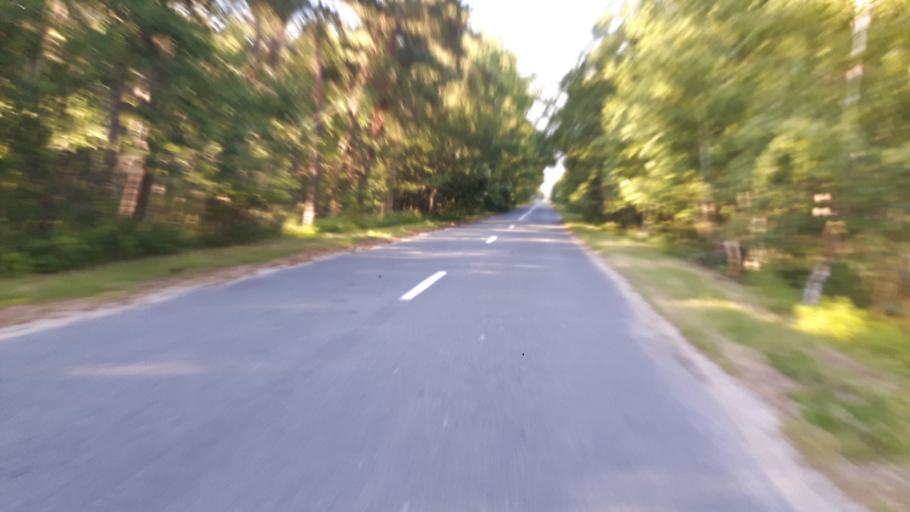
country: LT
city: Nida
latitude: 55.2602
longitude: 20.9389
